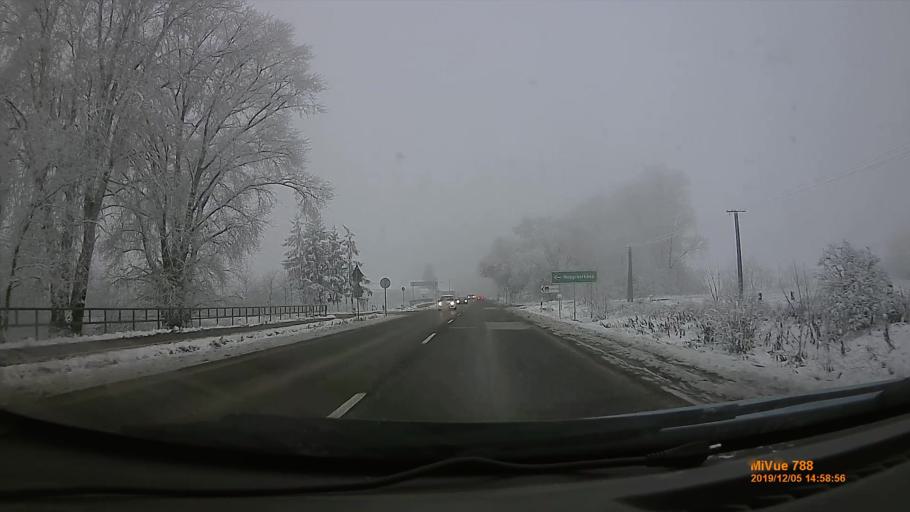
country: HU
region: Szabolcs-Szatmar-Bereg
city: Nyirtelek
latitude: 48.0531
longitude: 21.5642
